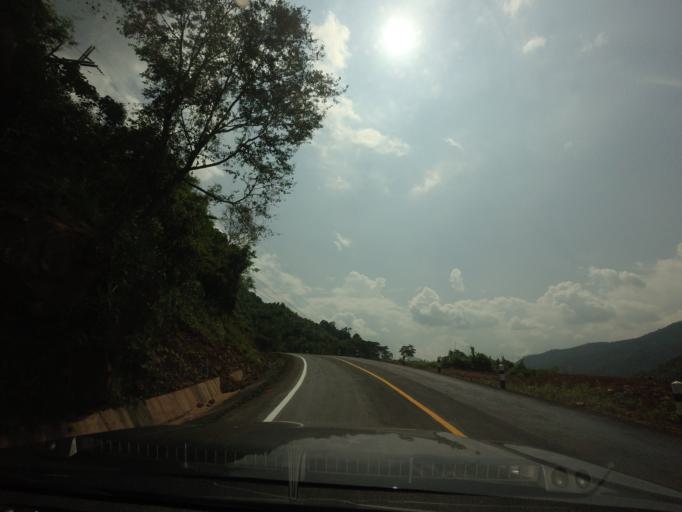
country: TH
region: Nan
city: Bo Kluea
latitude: 19.1719
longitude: 101.1702
